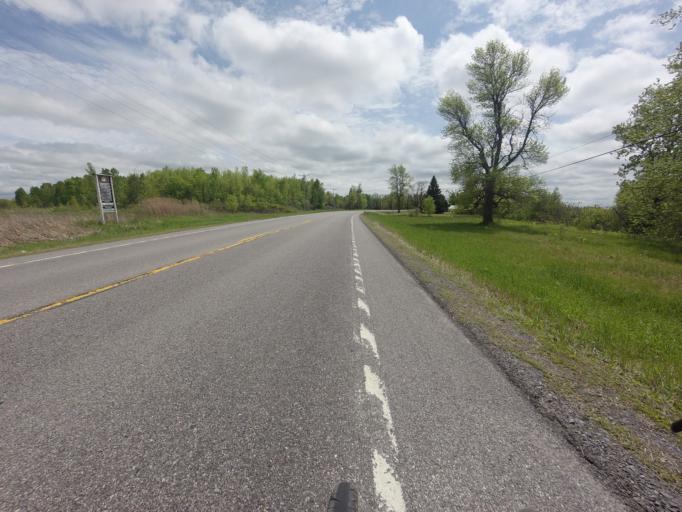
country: CA
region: Ontario
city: Cornwall
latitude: 44.9628
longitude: -74.6659
